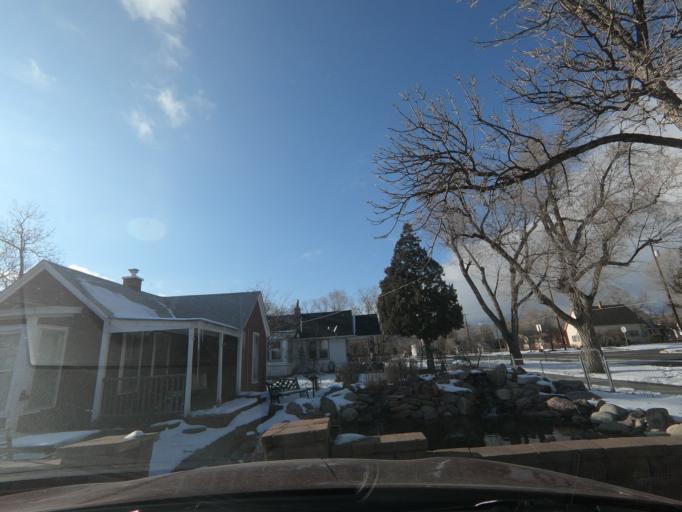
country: US
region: Colorado
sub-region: El Paso County
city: Colorado Springs
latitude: 38.8416
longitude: -104.8651
